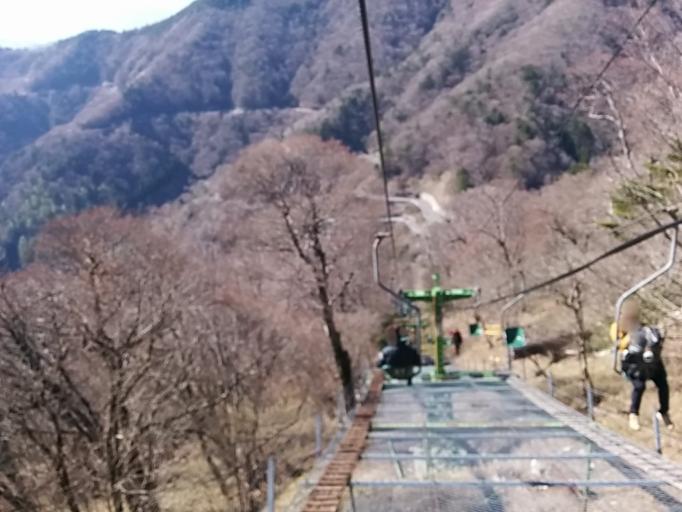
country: JP
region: Tokushima
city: Wakimachi
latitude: 33.8644
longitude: 134.0901
